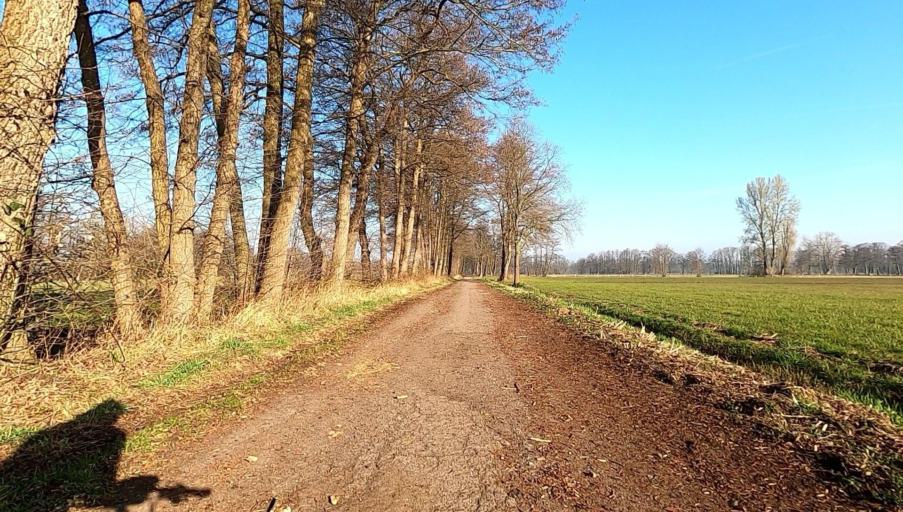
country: DE
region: Lower Saxony
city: Garbsen-Mitte
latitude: 52.4545
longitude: 9.6421
